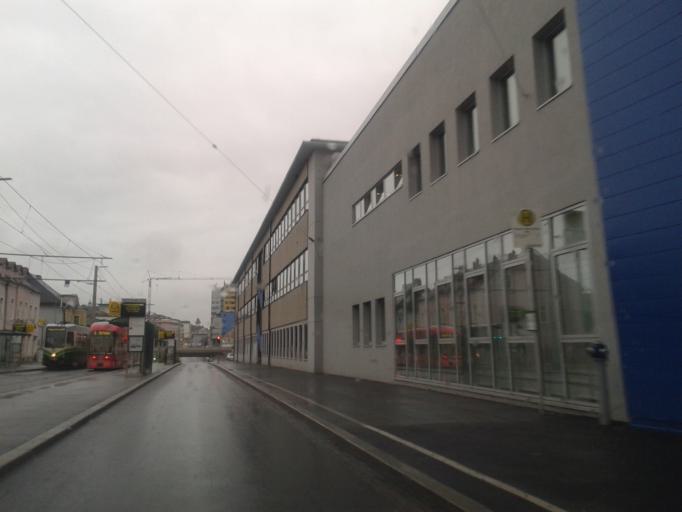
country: AT
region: Styria
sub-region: Graz Stadt
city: Wetzelsdorf
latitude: 47.0705
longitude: 15.4134
